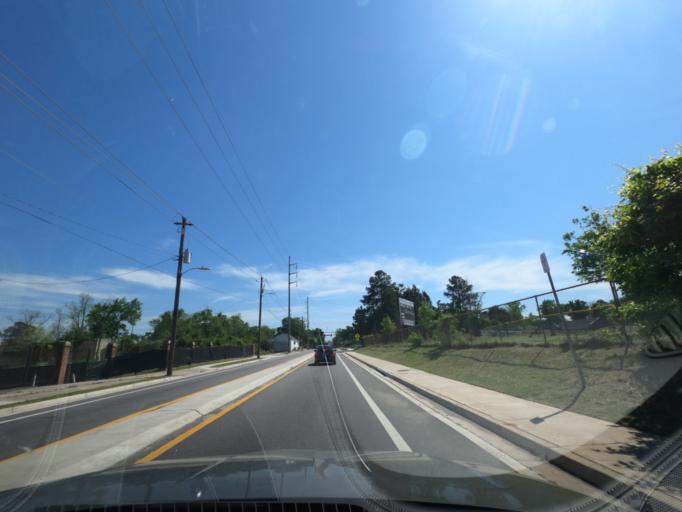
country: US
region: Georgia
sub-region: Richmond County
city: Augusta
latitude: 33.4691
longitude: -81.9966
